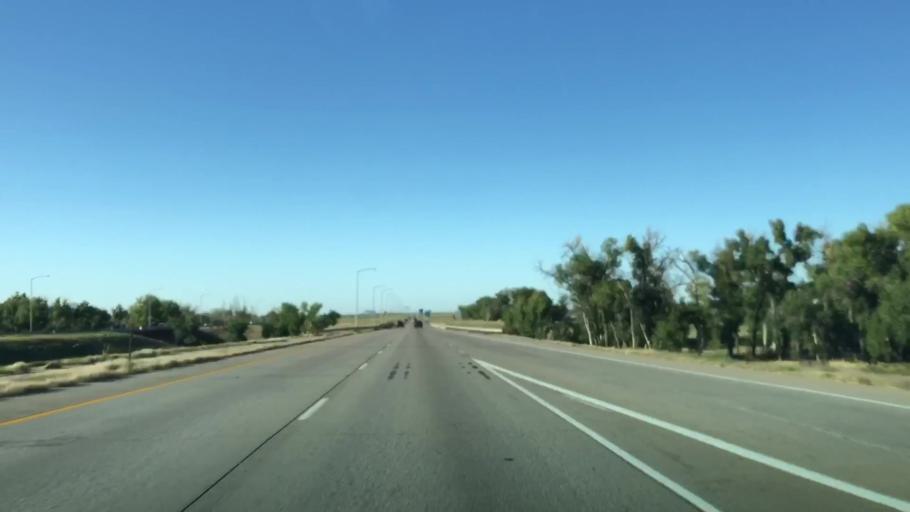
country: US
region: Colorado
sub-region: Adams County
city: Aurora
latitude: 39.8019
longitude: -104.7863
